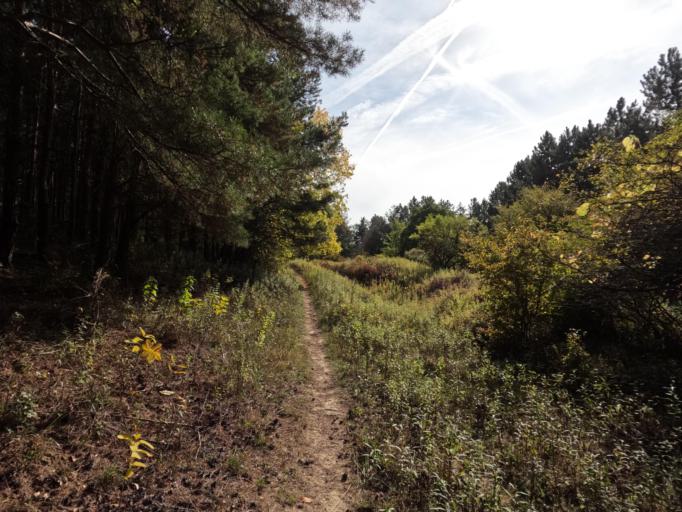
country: HU
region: Tolna
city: Szentgalpuszta
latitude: 46.3483
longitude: 18.6247
